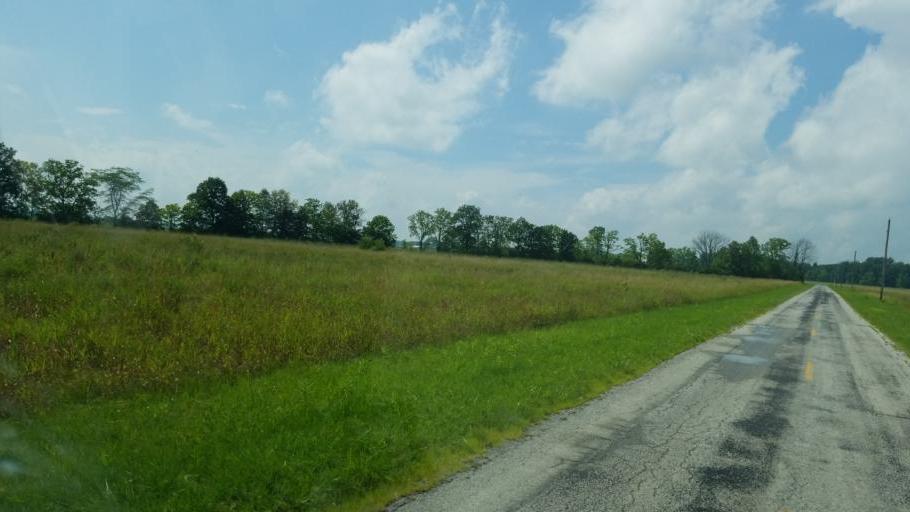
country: US
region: Ohio
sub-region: Union County
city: Richwood
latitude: 40.5615
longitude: -83.3417
